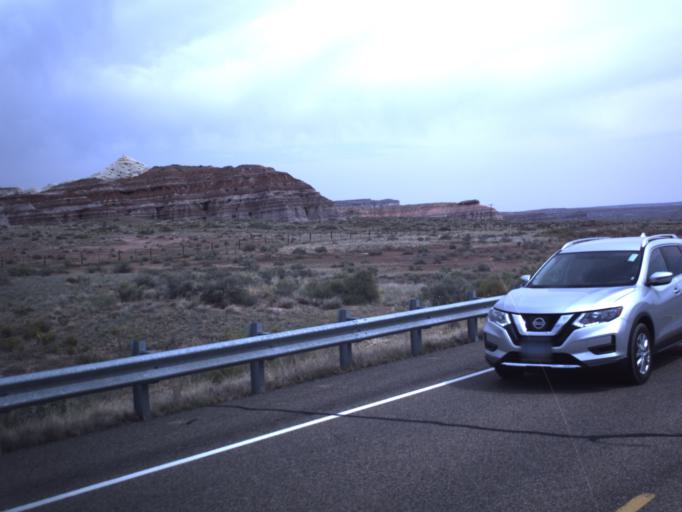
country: US
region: Arizona
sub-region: Coconino County
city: Page
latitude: 37.1205
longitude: -111.9430
